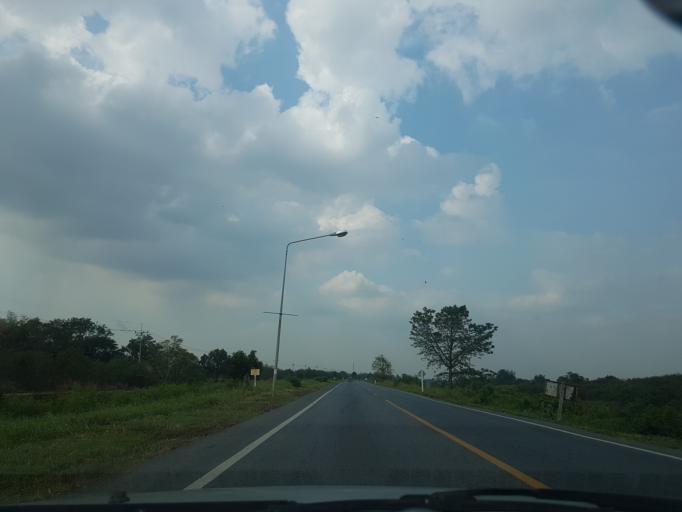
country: TH
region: Phra Nakhon Si Ayutthaya
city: Phachi
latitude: 14.4788
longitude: 100.7426
